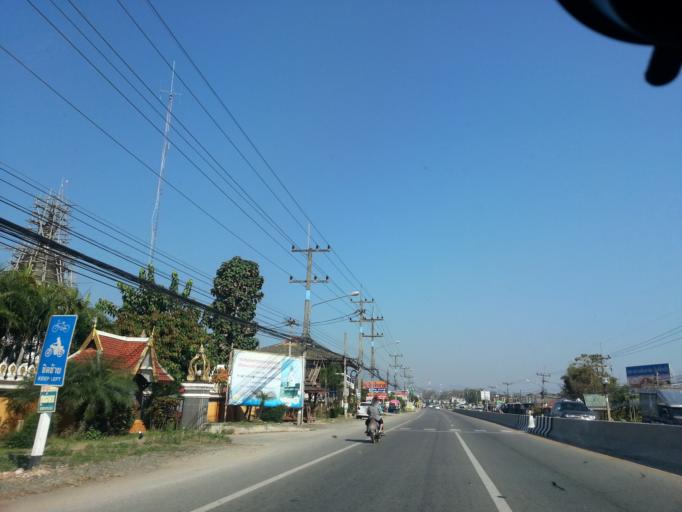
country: TH
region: Chiang Mai
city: Mae Taeng
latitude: 19.0868
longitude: 98.9369
